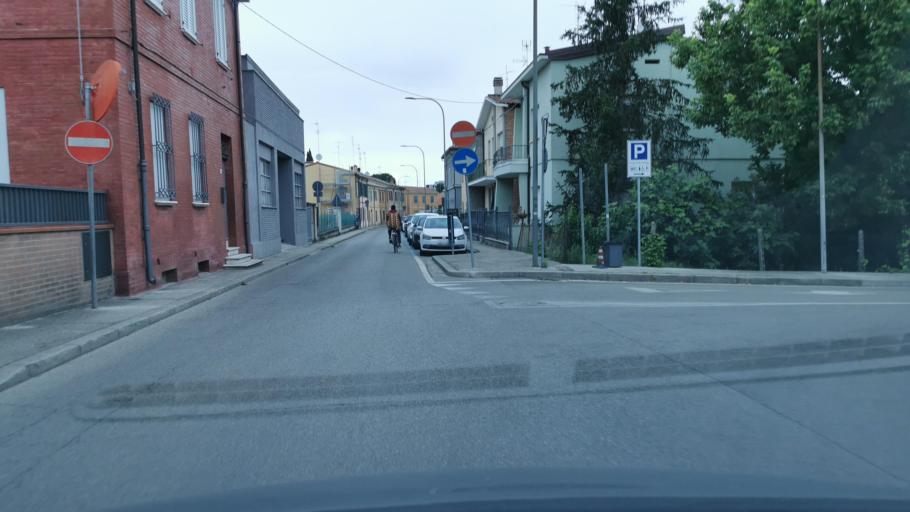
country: IT
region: Emilia-Romagna
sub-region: Provincia di Ravenna
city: Ravenna
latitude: 44.4213
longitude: 12.1948
